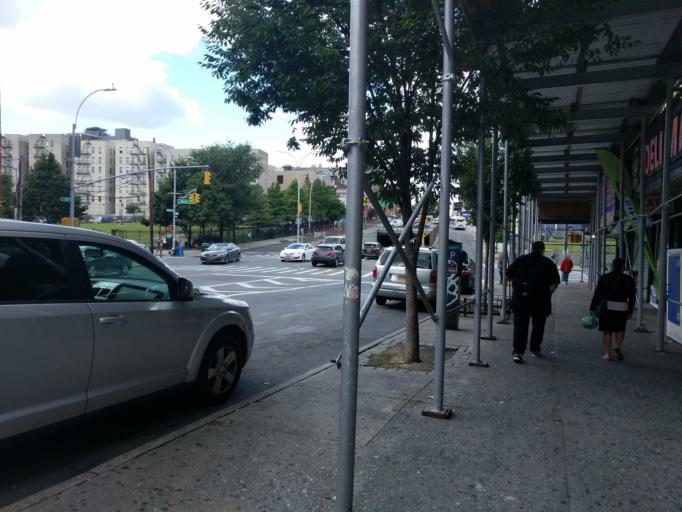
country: US
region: New York
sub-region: New York County
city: Inwood
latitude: 40.8378
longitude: -73.9110
